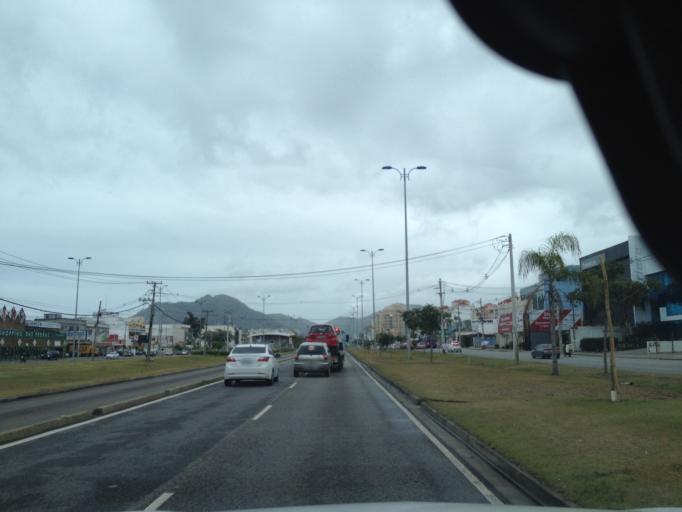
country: BR
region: Rio de Janeiro
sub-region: Nilopolis
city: Nilopolis
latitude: -23.0136
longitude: -43.4642
